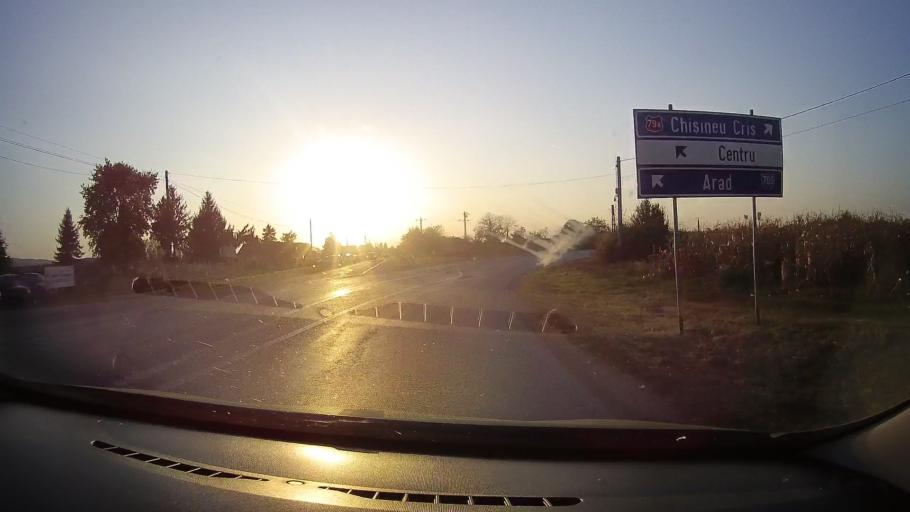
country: RO
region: Arad
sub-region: Comuna Ineu
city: Ineu
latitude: 46.4280
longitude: 21.8638
